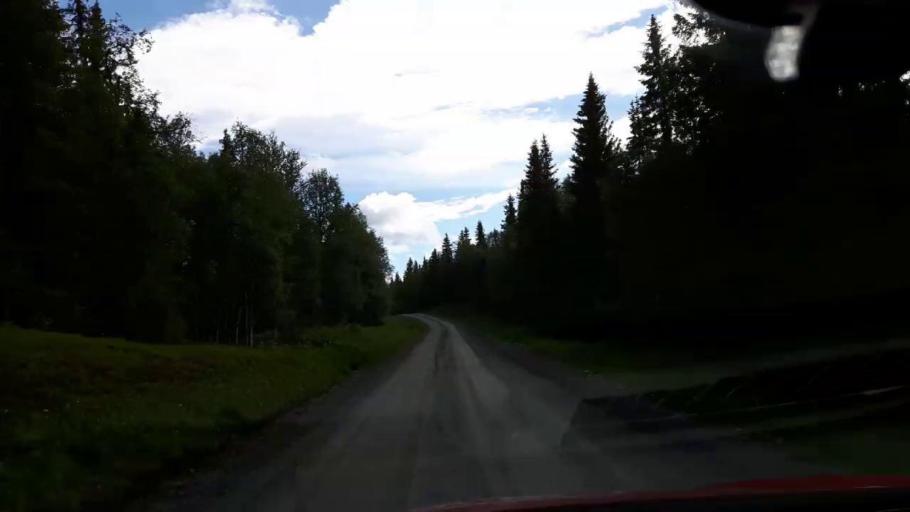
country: SE
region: Jaemtland
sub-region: Krokoms Kommun
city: Valla
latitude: 63.8747
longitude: 14.1242
